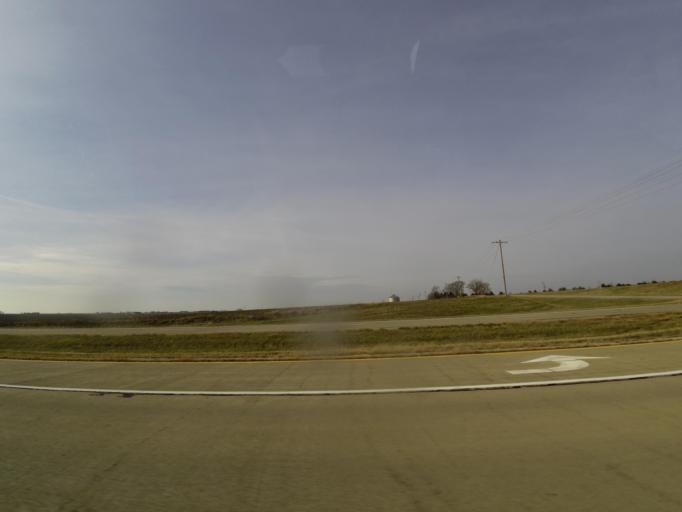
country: US
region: Illinois
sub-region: McLean County
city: Heyworth
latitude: 40.3851
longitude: -88.9893
